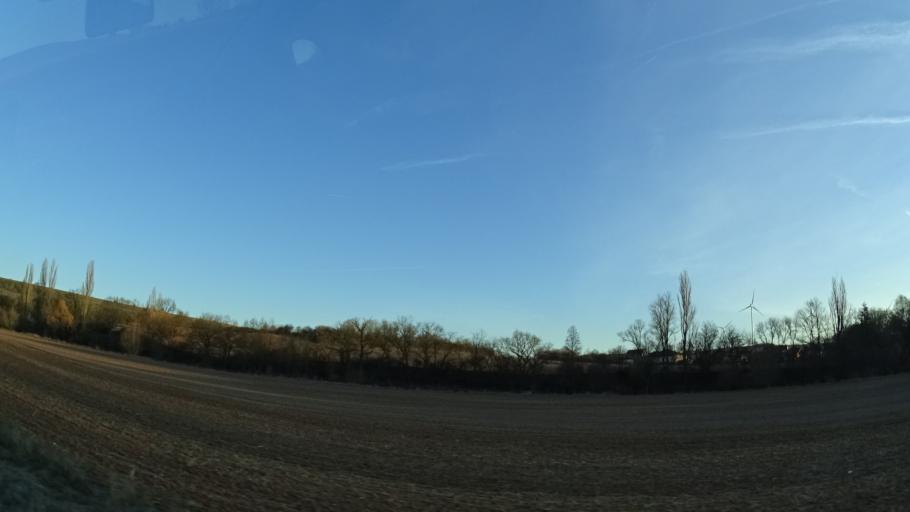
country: DE
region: Rheinland-Pfalz
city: Bolanden
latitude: 49.6354
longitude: 8.0238
